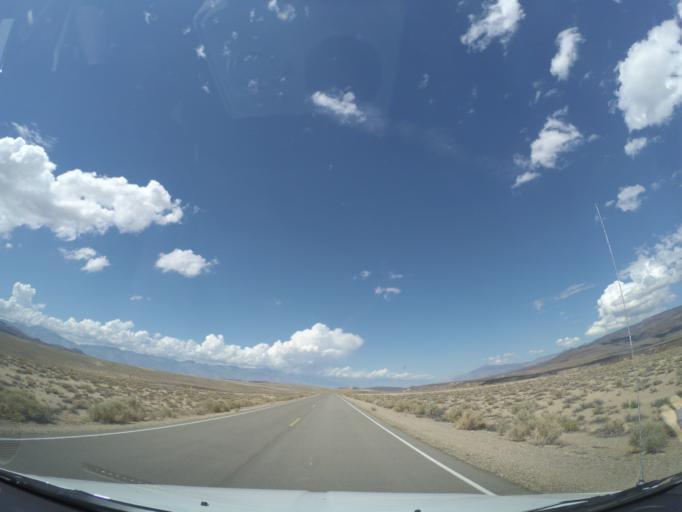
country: US
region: California
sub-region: Inyo County
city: Lone Pine
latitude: 36.3420
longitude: -117.7603
